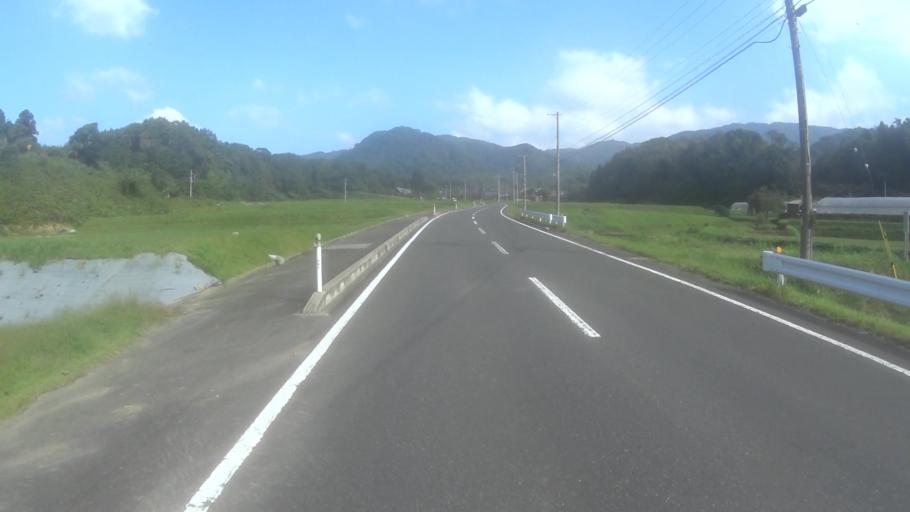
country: JP
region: Kyoto
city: Miyazu
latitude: 35.6029
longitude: 135.1464
